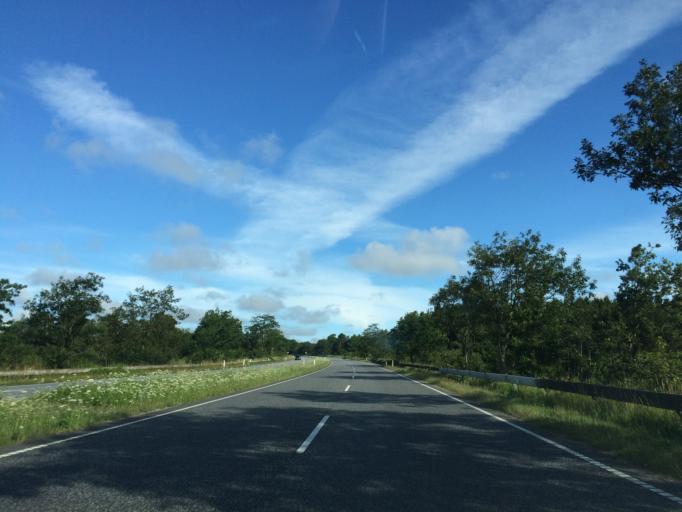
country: DK
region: Central Jutland
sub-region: Viborg Kommune
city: Viborg
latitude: 56.4050
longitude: 9.4333
